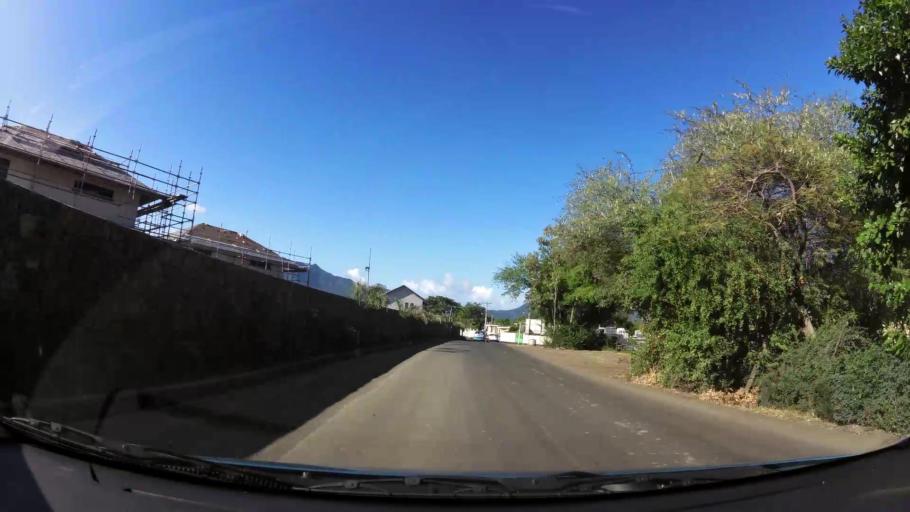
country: MU
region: Black River
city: Grande Riviere Noire
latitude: -20.3555
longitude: 57.3666
